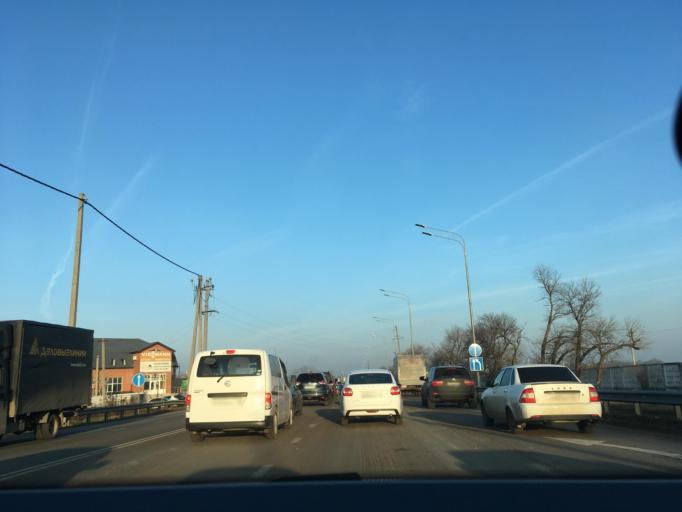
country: RU
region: Krasnodarskiy
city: Krasnodar
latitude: 45.1288
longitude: 39.0152
